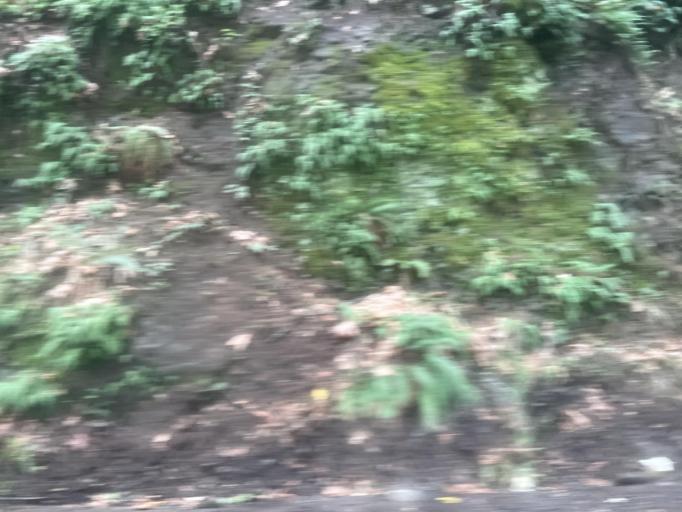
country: US
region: Washington
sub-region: Clark County
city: Washougal
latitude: 45.5486
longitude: -122.1952
